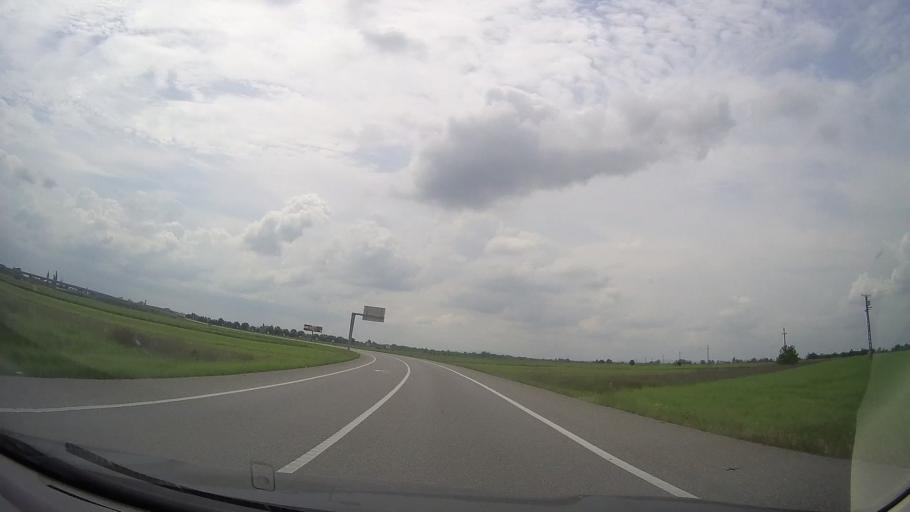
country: RO
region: Timis
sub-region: Comuna Costeiu
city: Costeiu
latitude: 45.7258
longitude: 21.8699
